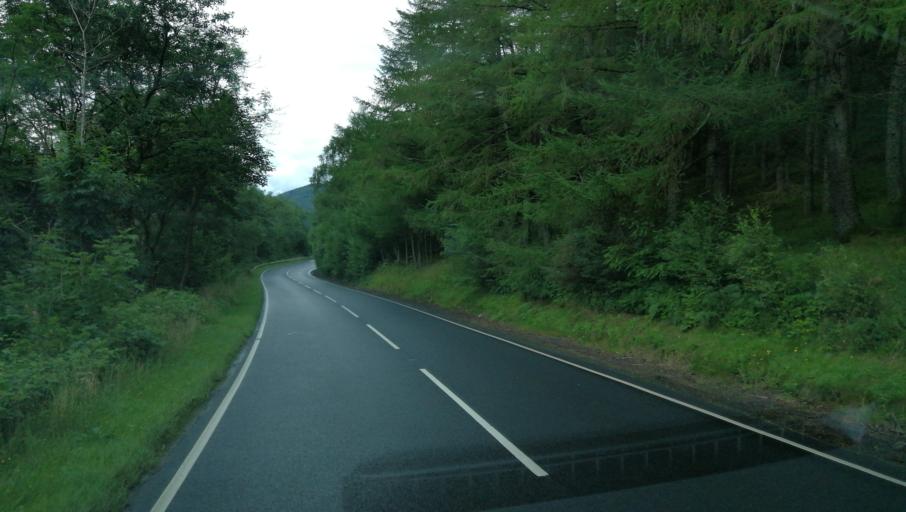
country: GB
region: Scotland
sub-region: Stirling
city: Callander
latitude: 56.2680
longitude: -4.2845
